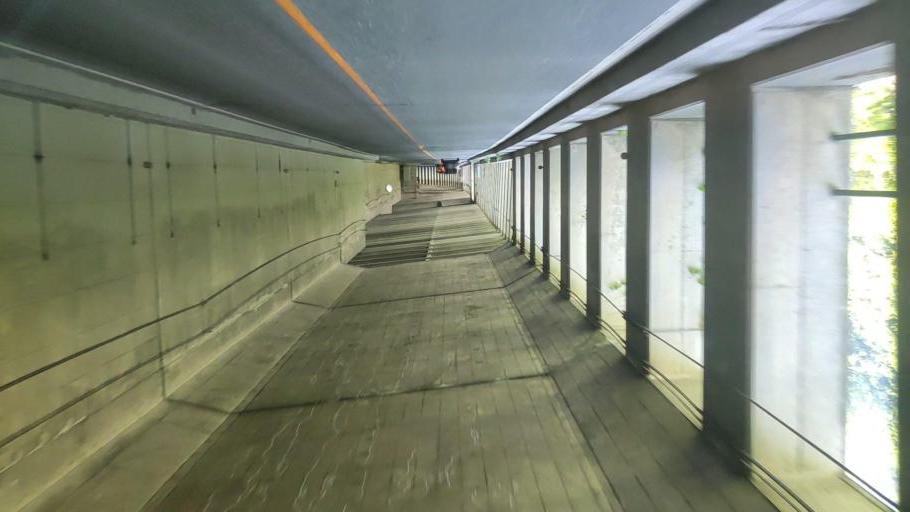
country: JP
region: Niigata
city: Itoigawa
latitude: 36.9118
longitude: 137.8629
